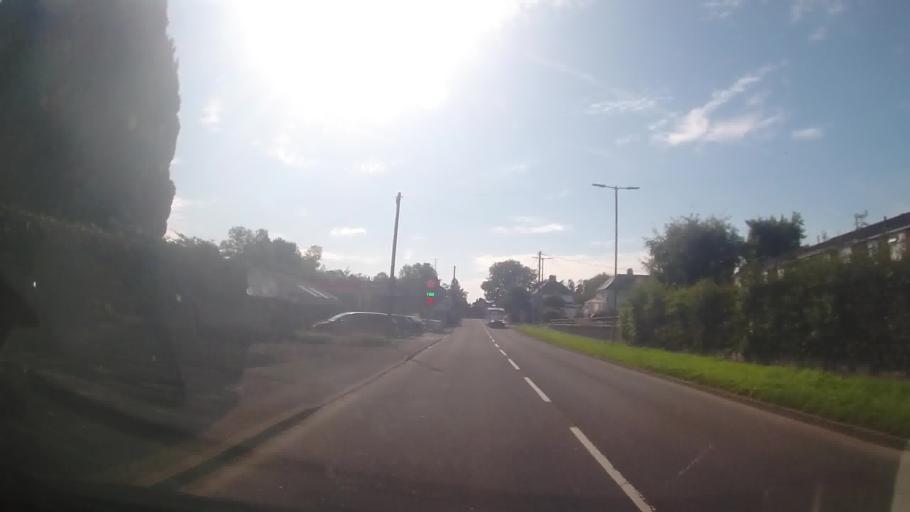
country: GB
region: Wales
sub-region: Sir Powys
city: Rhayader
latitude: 52.3032
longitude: -3.5040
